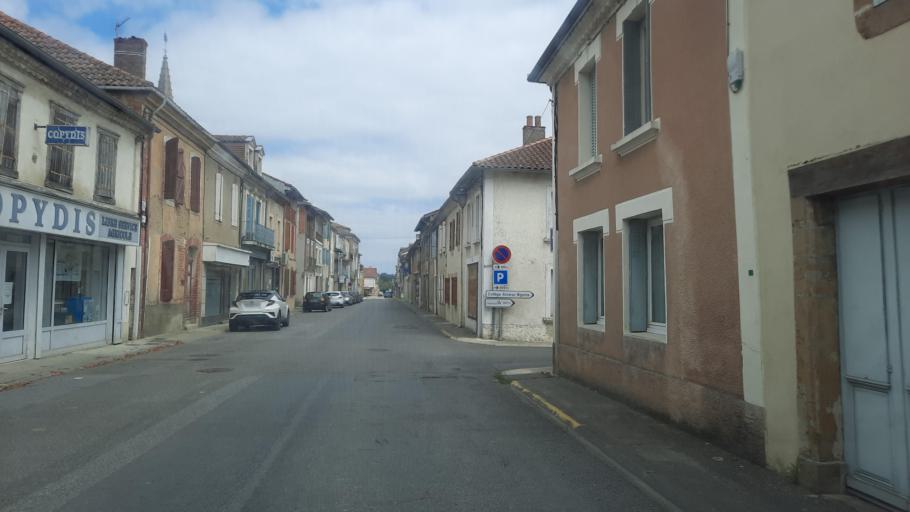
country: FR
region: Midi-Pyrenees
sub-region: Departement des Hautes-Pyrenees
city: Trie-sur-Baise
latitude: 43.3192
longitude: 0.3692
